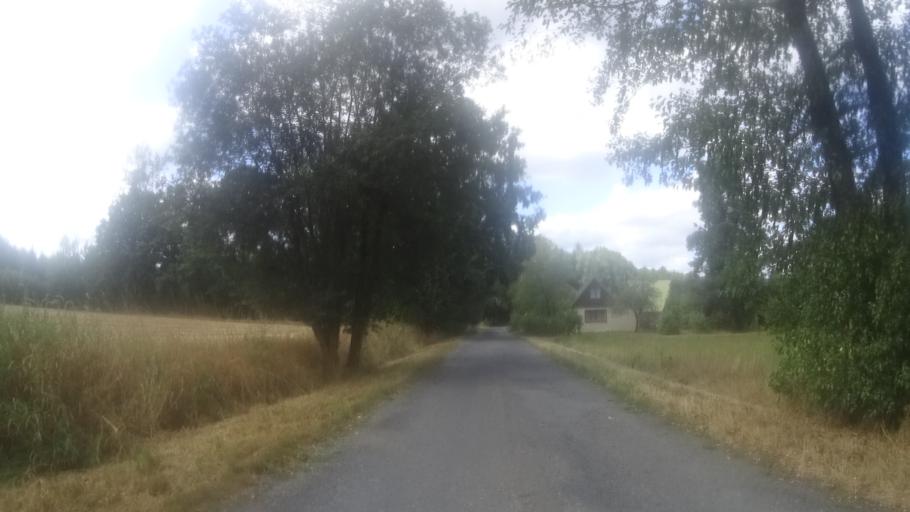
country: CZ
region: Pardubicky
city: Horni Jeleni
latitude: 50.0468
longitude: 16.1574
